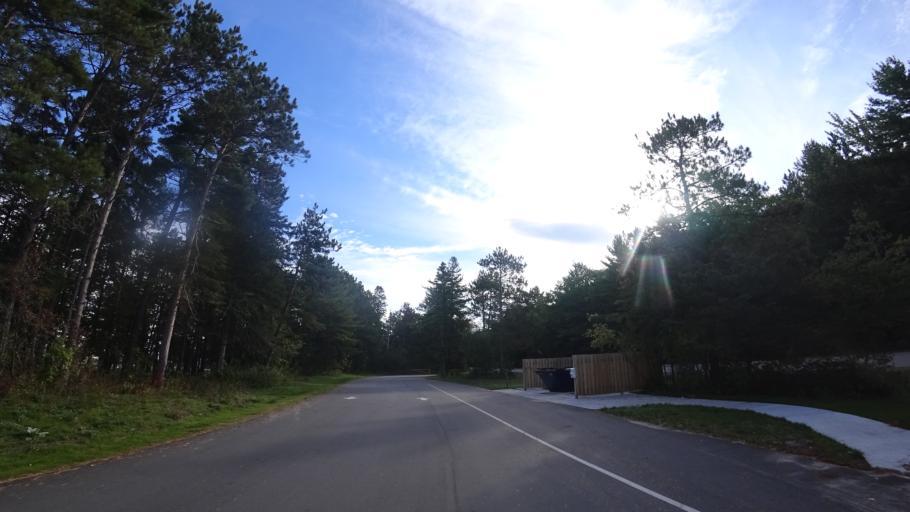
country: US
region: Michigan
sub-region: Mackinac County
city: Saint Ignace
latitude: 45.7457
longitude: -84.9021
